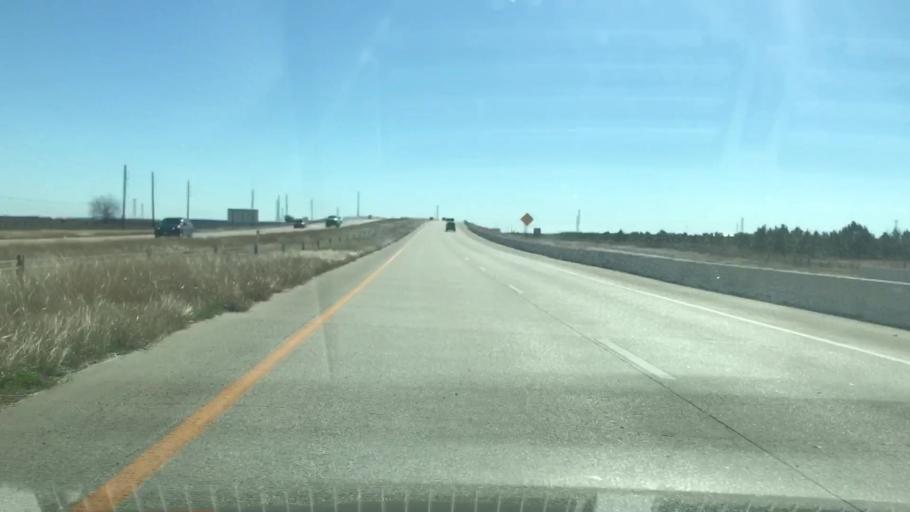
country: US
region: Texas
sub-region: Harris County
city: Cypress
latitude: 29.9258
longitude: -95.7626
